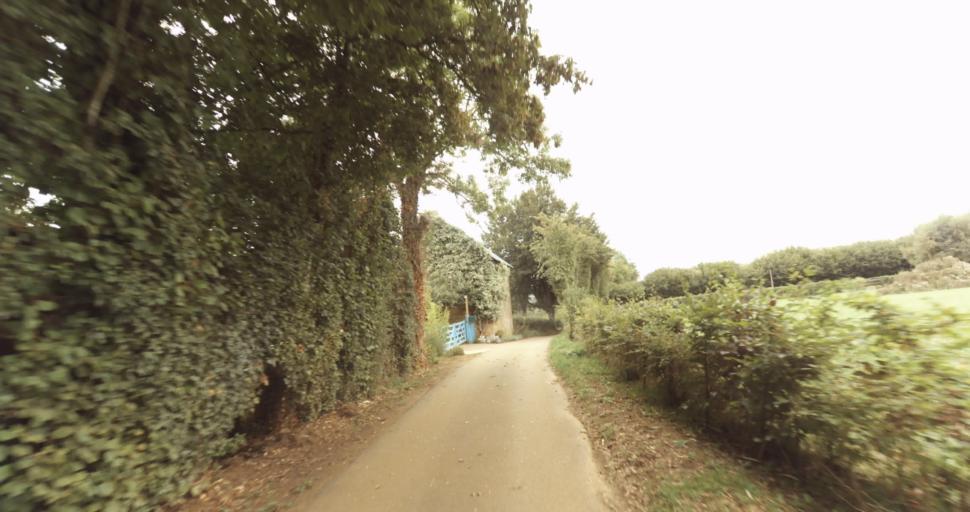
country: FR
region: Lower Normandy
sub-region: Departement de l'Orne
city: Gace
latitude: 48.7584
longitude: 0.3256
